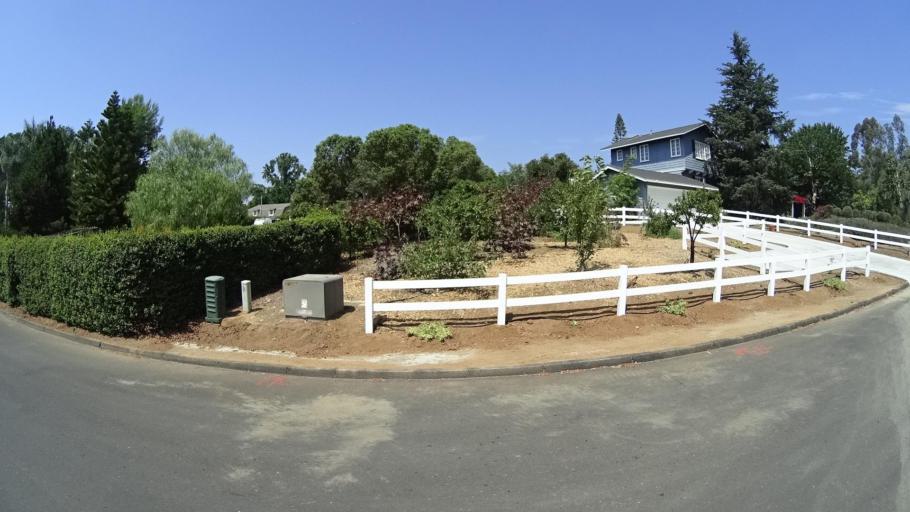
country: US
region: California
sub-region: San Diego County
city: Fallbrook
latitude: 33.3641
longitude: -117.2376
